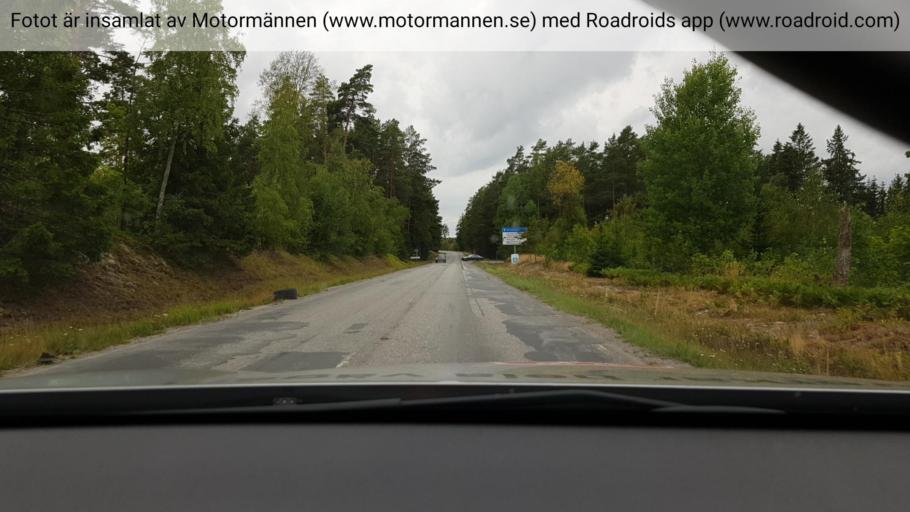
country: SE
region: Stockholm
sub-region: Sigtuna Kommun
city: Rosersberg
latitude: 59.6217
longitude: 17.9305
